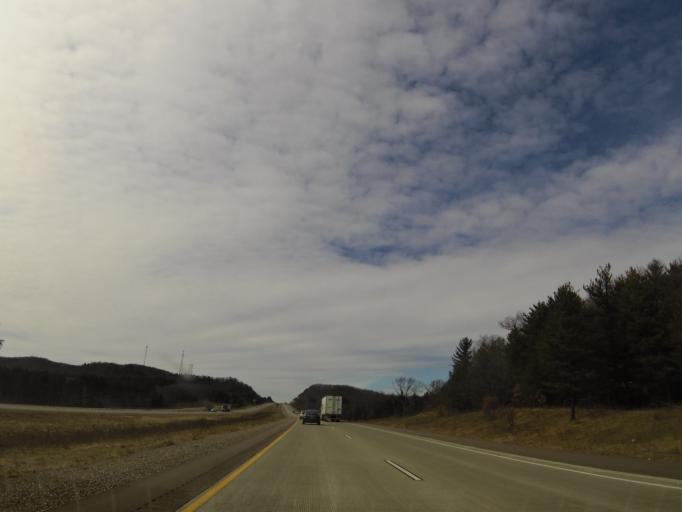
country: US
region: Wisconsin
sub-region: Jackson County
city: Black River Falls
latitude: 44.3313
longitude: -90.8946
